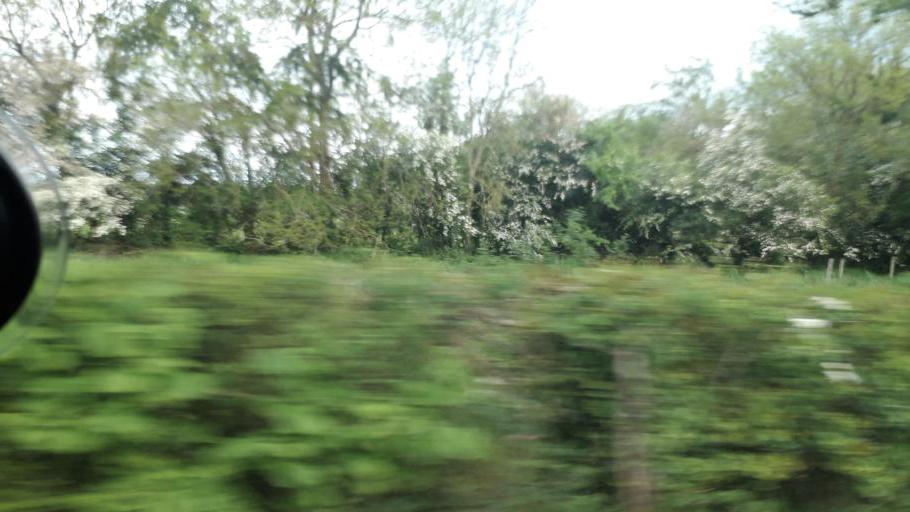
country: IE
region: Leinster
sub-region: Kildare
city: Celbridge
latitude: 53.3049
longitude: -6.5581
